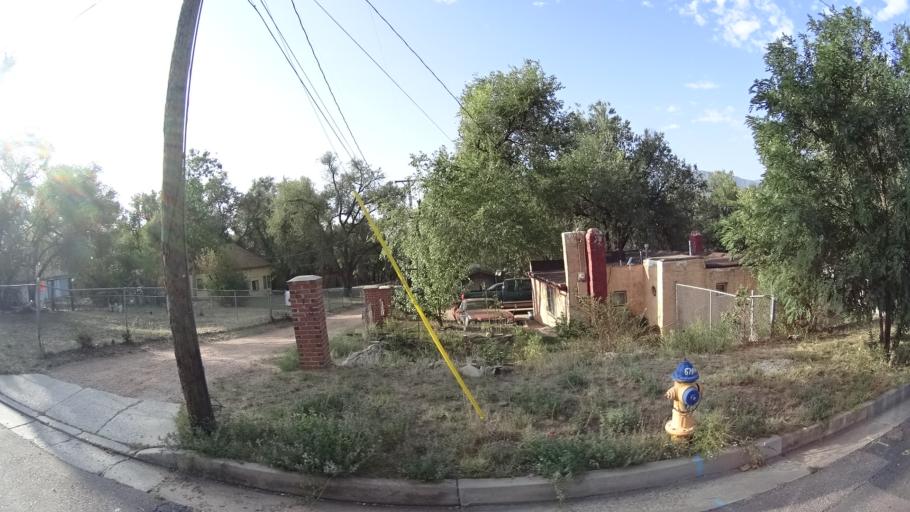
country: US
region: Colorado
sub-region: El Paso County
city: Colorado Springs
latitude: 38.8188
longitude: -104.8147
